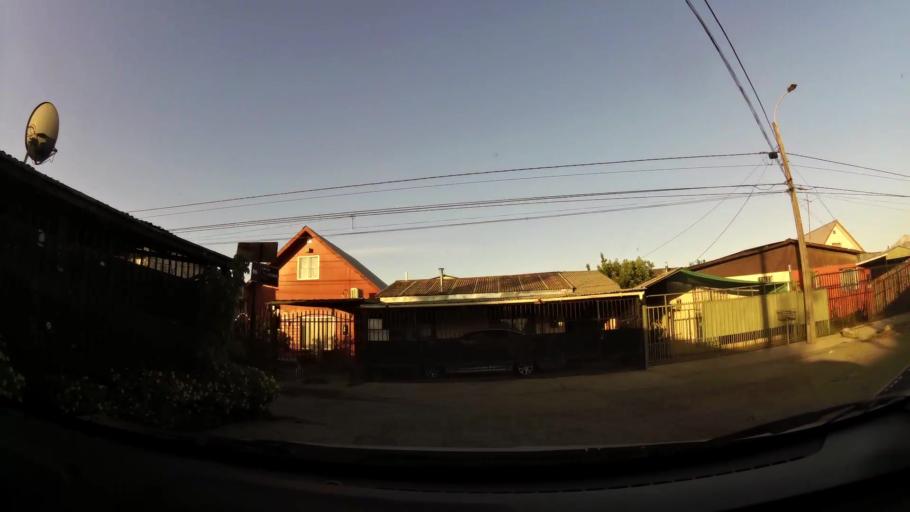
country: CL
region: Maule
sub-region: Provincia de Talca
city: Talca
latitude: -35.4412
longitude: -71.6380
